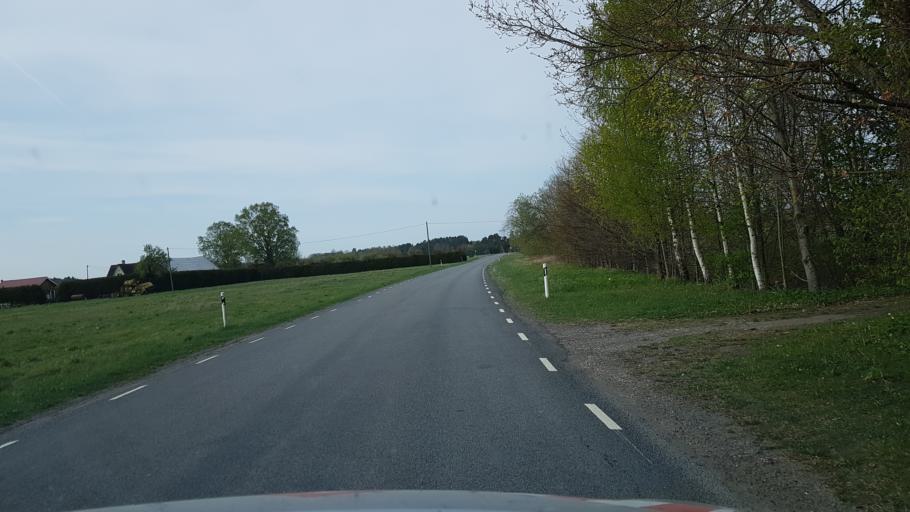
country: EE
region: Paernumaa
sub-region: Audru vald
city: Audru
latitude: 58.3635
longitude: 24.2630
